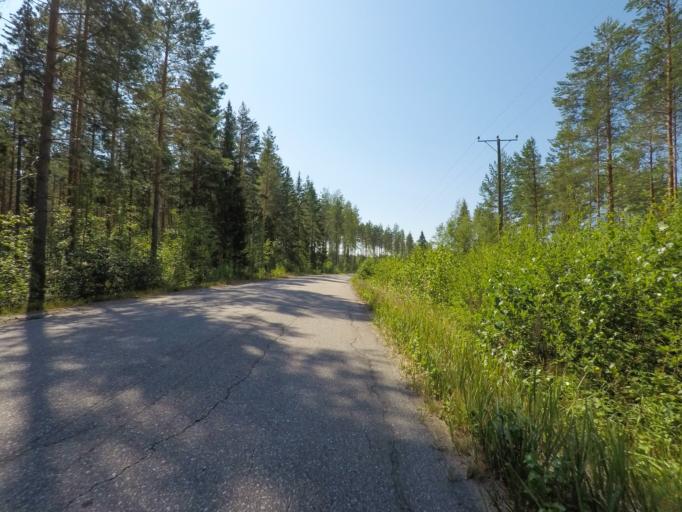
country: FI
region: Southern Savonia
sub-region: Mikkeli
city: Puumala
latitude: 61.4250
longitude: 28.1568
